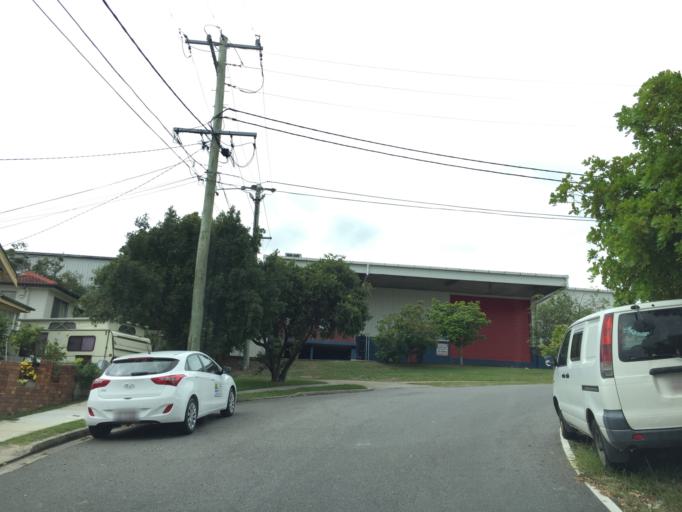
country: AU
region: Queensland
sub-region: Brisbane
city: Grange
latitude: -27.4258
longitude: 153.0045
